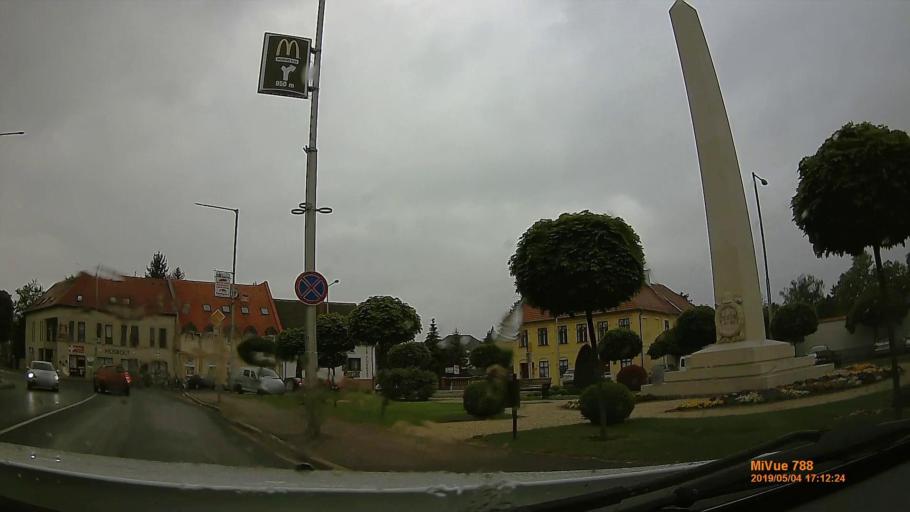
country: HU
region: Gyor-Moson-Sopron
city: Mosonmagyarovar
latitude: 47.8764
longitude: 17.2681
